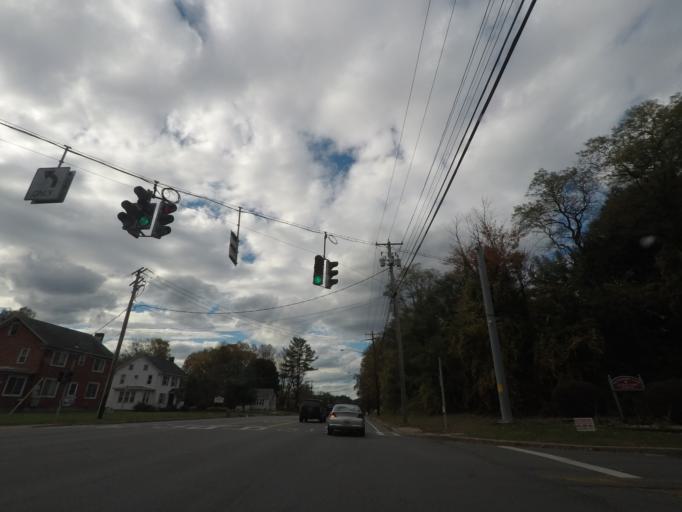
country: US
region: New York
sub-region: Albany County
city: Westmere
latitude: 42.7003
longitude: -73.9022
